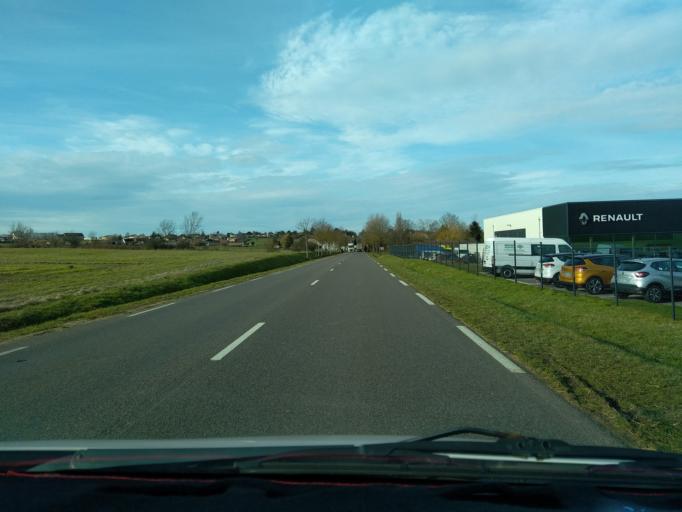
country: FR
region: Franche-Comte
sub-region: Departement de la Haute-Saone
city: Gray
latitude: 47.4306
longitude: 5.6061
